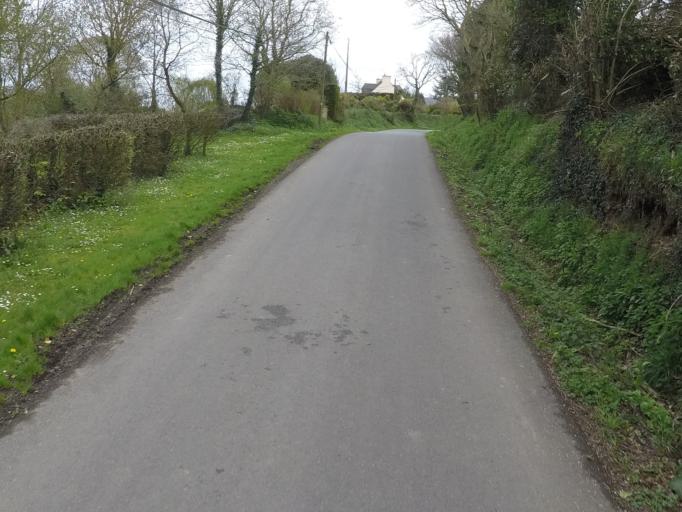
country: FR
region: Brittany
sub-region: Departement des Cotes-d'Armor
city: Plouha
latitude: 48.7035
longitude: -2.9343
